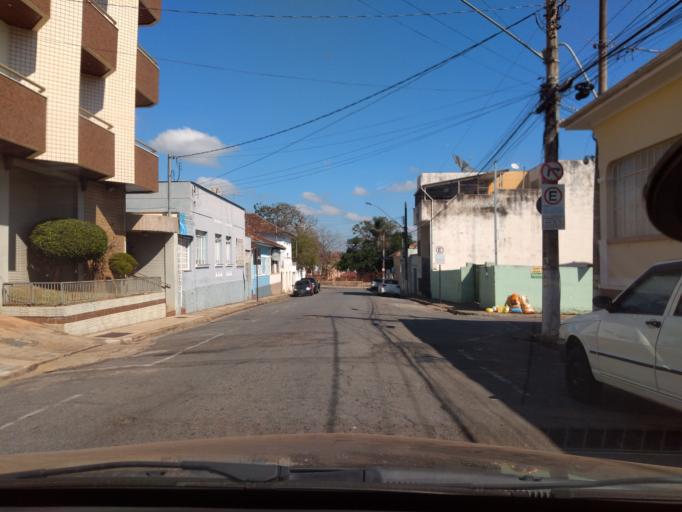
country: BR
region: Minas Gerais
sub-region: Tres Coracoes
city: Tres Coracoes
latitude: -21.6981
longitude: -45.2525
